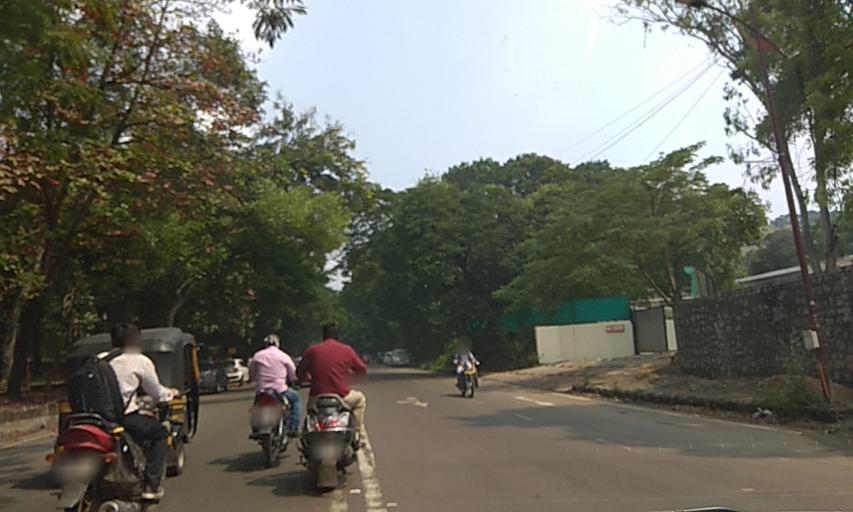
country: IN
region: Maharashtra
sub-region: Pune Division
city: Shivaji Nagar
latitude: 18.5402
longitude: 73.8185
